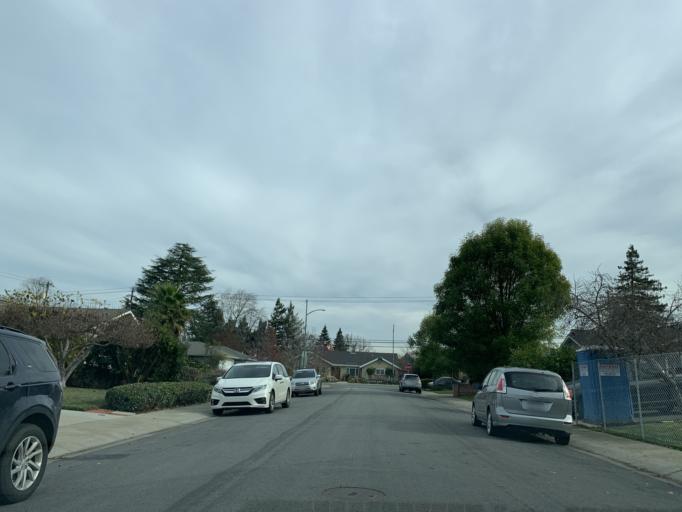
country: US
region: California
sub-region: Santa Clara County
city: Mountain View
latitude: 37.3850
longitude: -122.0912
